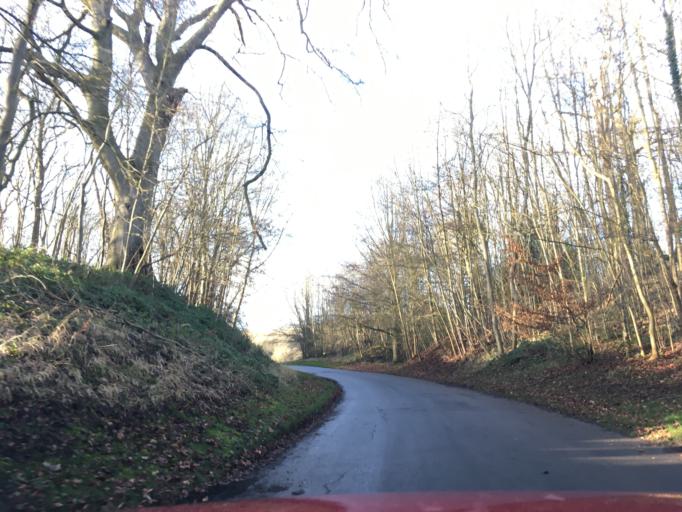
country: GB
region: England
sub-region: Warwickshire
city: Stratford-upon-Avon
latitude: 52.2059
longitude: -1.6953
